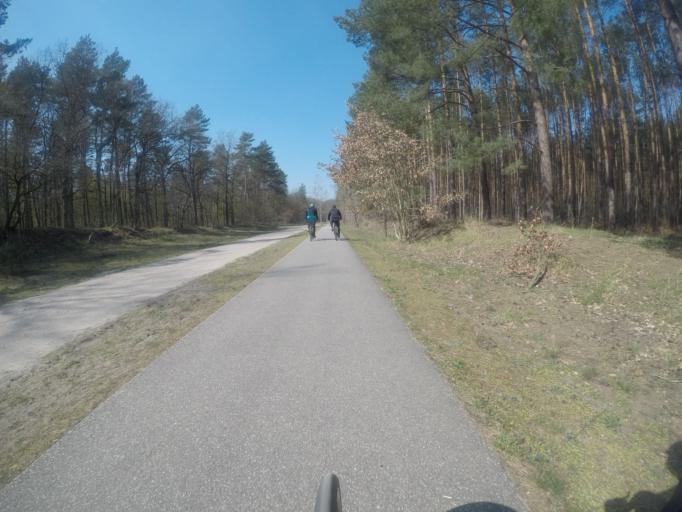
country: DE
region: Brandenburg
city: Hennigsdorf
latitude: 52.6405
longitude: 13.1751
